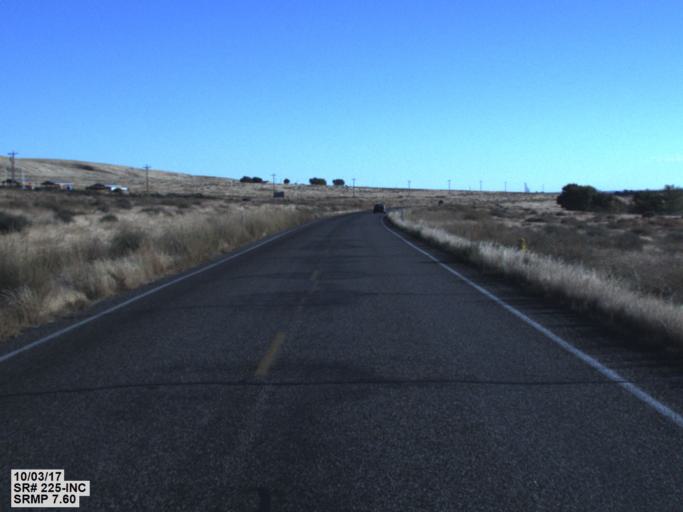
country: US
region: Washington
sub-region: Benton County
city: Benton City
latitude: 46.3469
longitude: -119.4700
